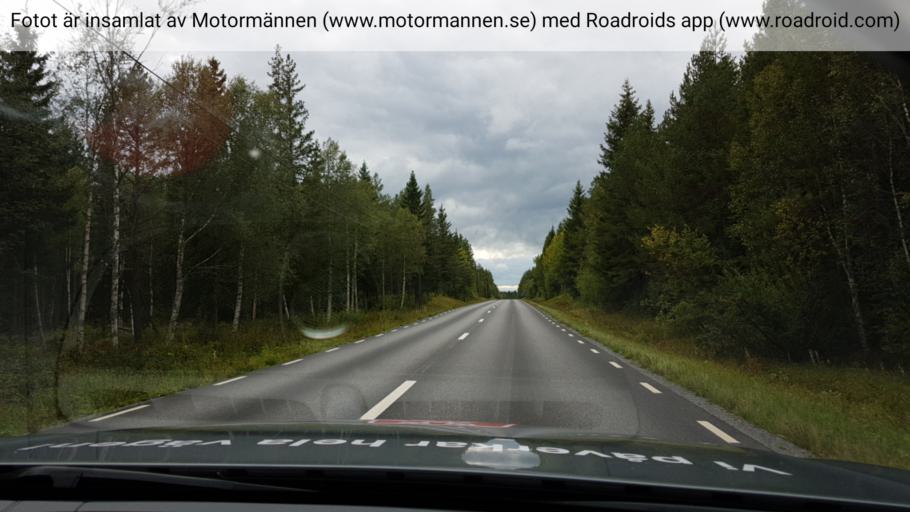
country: SE
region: Jaemtland
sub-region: Bergs Kommun
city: Hoverberg
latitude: 62.9681
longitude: 14.5419
